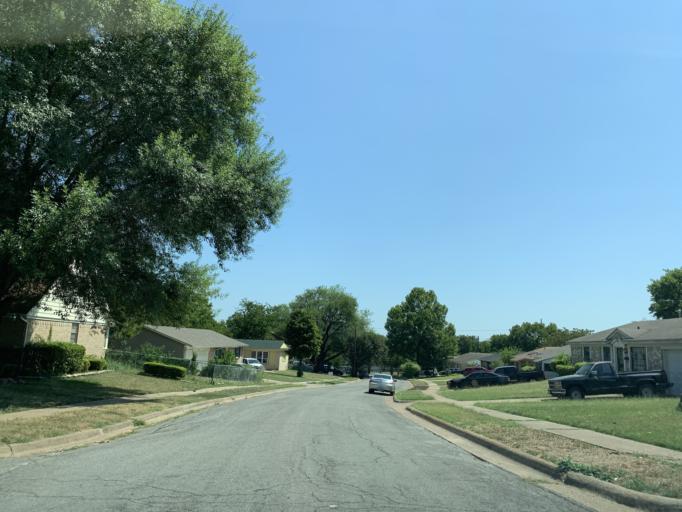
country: US
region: Texas
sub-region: Dallas County
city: Hutchins
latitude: 32.6760
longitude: -96.7501
